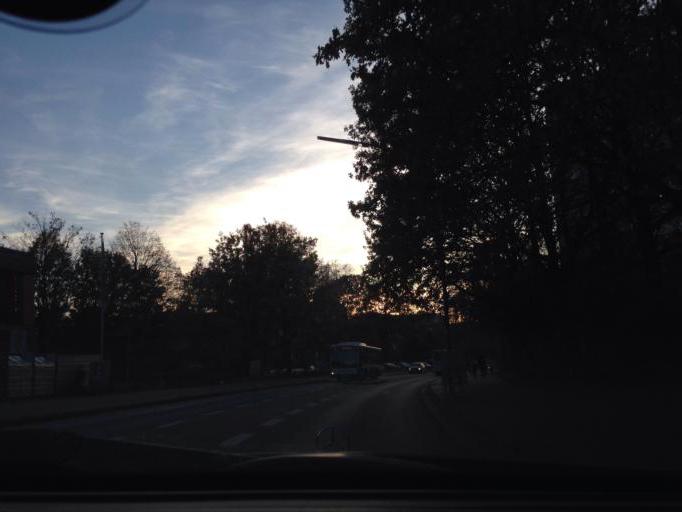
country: DE
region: Schleswig-Holstein
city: Barsbuettel
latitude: 53.5843
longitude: 10.1457
